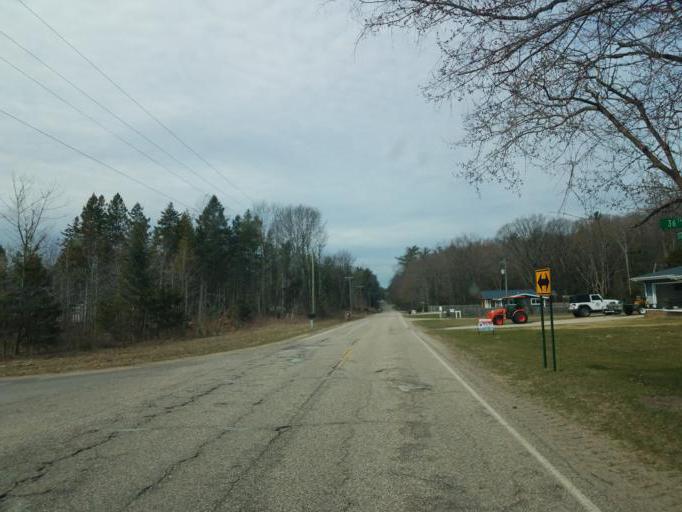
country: US
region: Michigan
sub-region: Oceana County
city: Shelby
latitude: 43.5555
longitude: -86.4672
